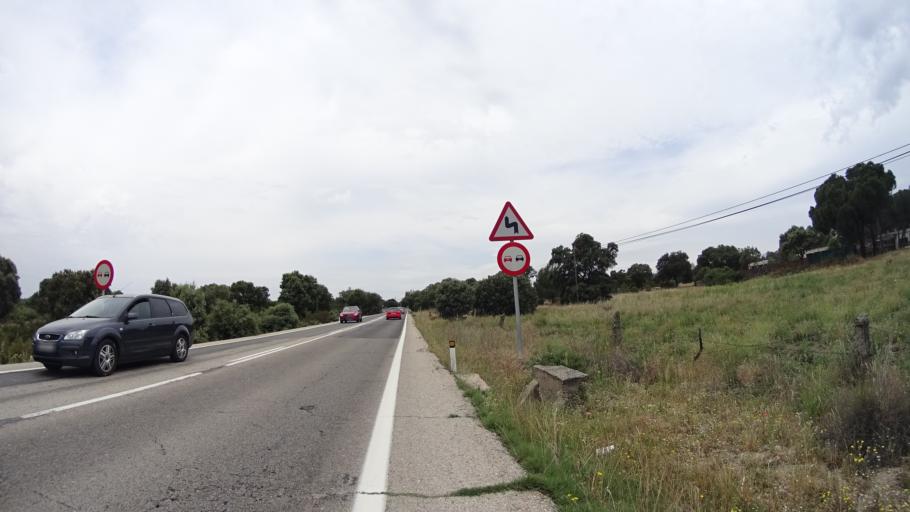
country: ES
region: Madrid
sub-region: Provincia de Madrid
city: Colmenarejo
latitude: 40.5436
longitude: -4.0387
